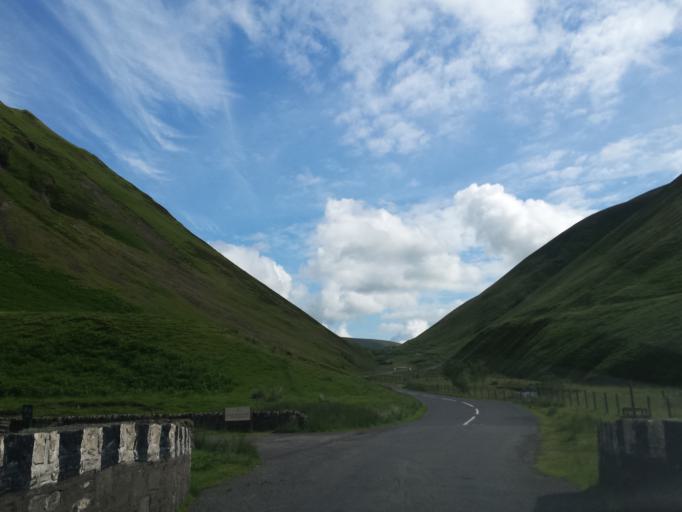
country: GB
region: Scotland
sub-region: Dumfries and Galloway
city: Moffat
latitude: 55.4177
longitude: -3.2866
